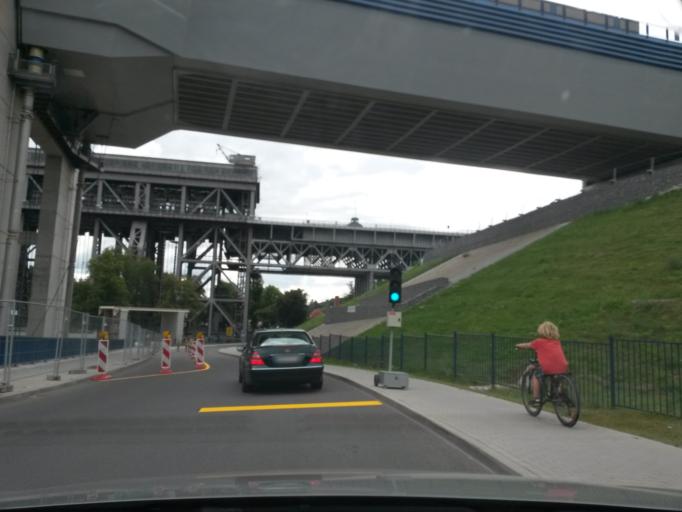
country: DE
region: Brandenburg
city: Niederfinow
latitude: 52.8508
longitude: 13.9416
